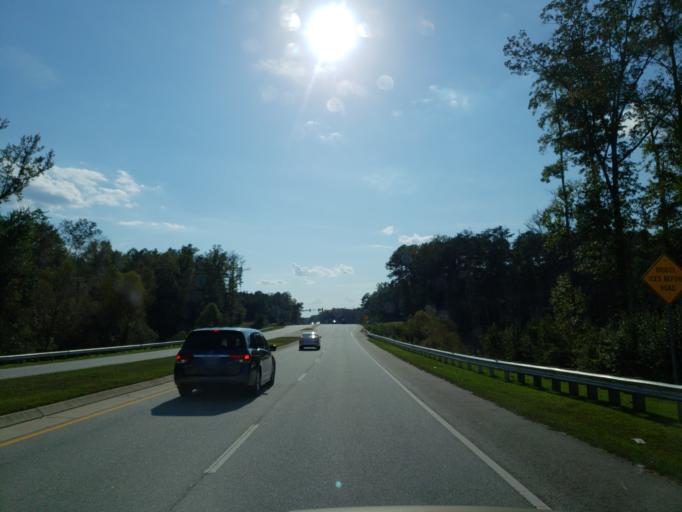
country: US
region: Georgia
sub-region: Paulding County
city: Hiram
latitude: 33.8622
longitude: -84.7456
